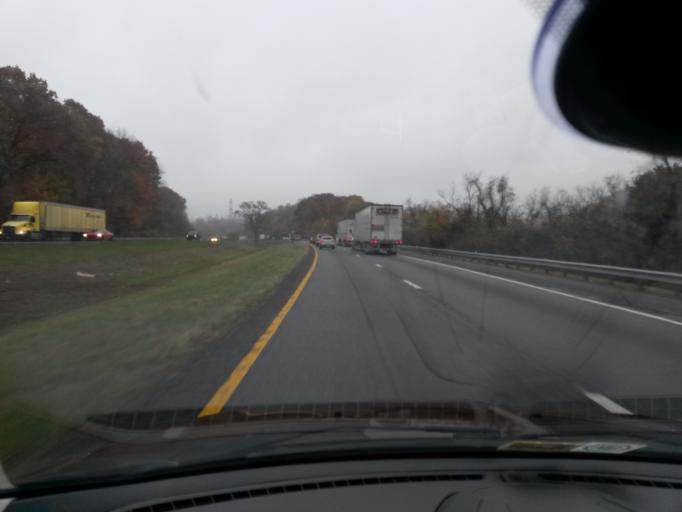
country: US
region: Virginia
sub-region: Montgomery County
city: Shawsville
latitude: 37.2501
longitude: -80.1885
